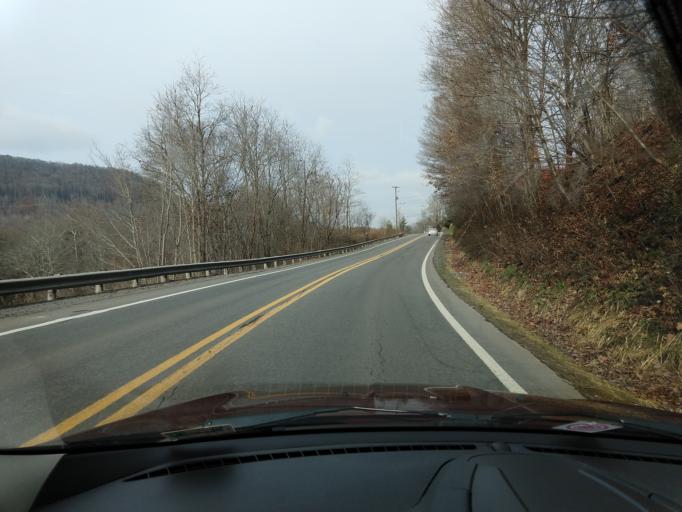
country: US
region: West Virginia
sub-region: Greenbrier County
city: Rainelle
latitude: 37.9691
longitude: -80.7043
